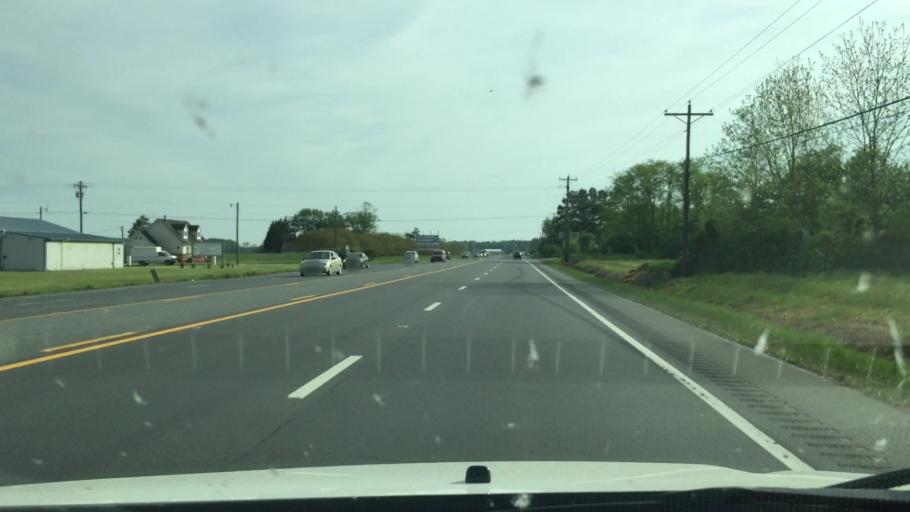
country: US
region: Virginia
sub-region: Accomack County
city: Accomac
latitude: 37.7451
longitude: -75.6376
